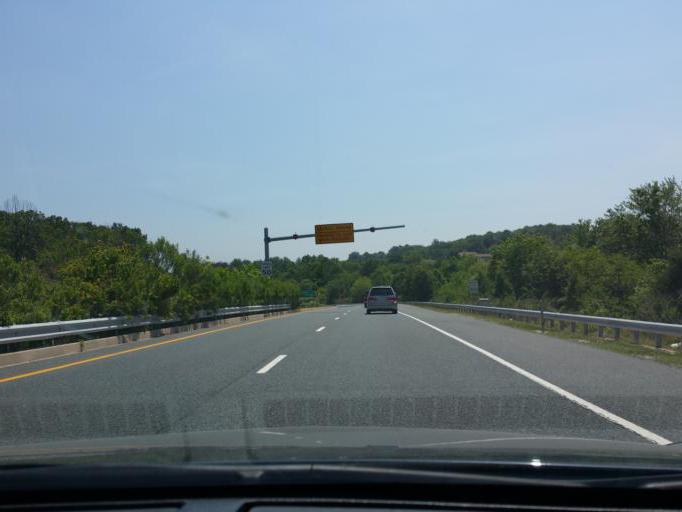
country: US
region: Maryland
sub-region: Baltimore County
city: Carney
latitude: 39.3814
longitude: -76.5185
